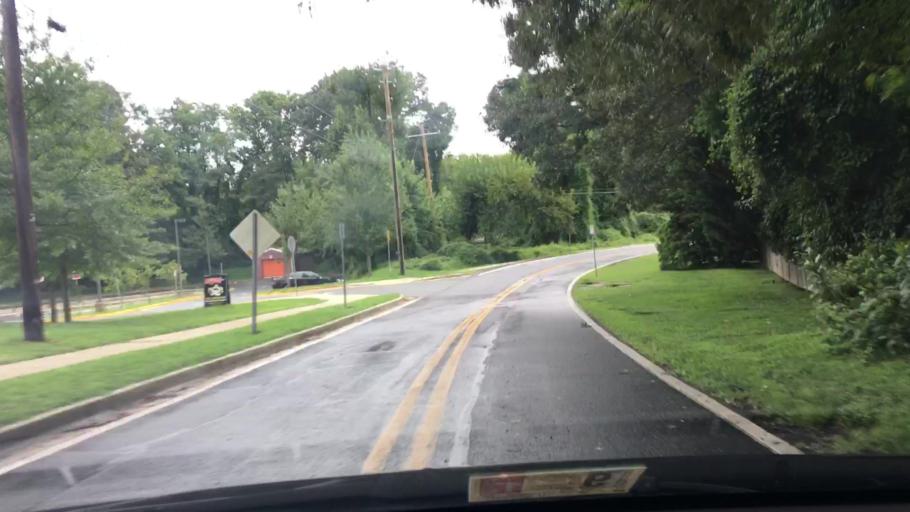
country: US
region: Maryland
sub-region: Montgomery County
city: Cabin John
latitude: 38.9832
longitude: -77.1725
